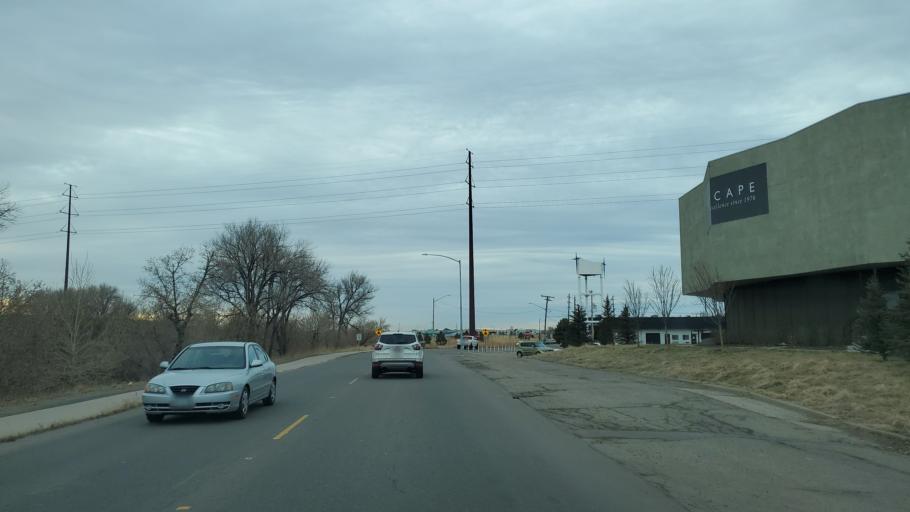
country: US
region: Colorado
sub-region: Denver County
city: Denver
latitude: 39.7088
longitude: -104.9996
